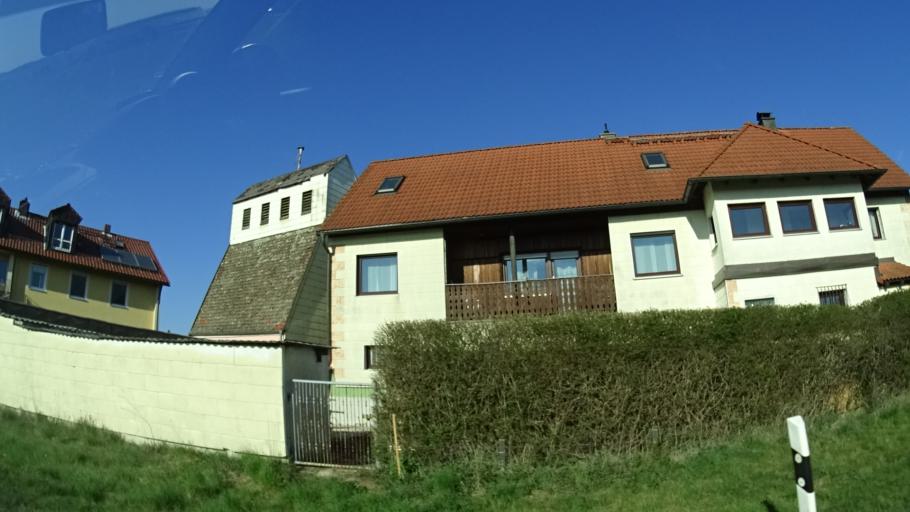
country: DE
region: Bavaria
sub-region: Upper Palatinate
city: Auerbach
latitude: 49.6820
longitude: 11.6374
